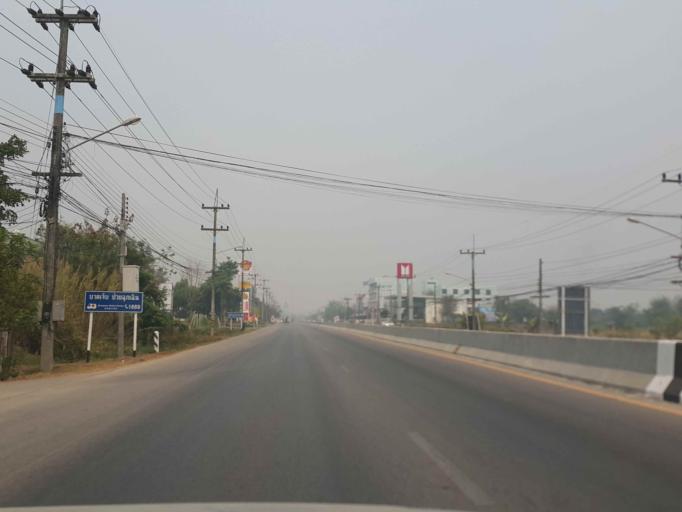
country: TH
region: Chiang Mai
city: Mae Taeng
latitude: 19.0743
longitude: 98.9383
